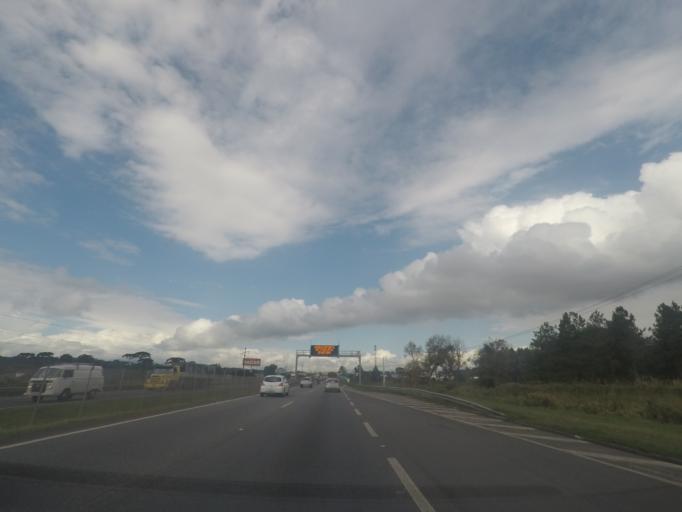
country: BR
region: Parana
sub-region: Piraquara
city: Piraquara
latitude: -25.5207
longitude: -49.1077
